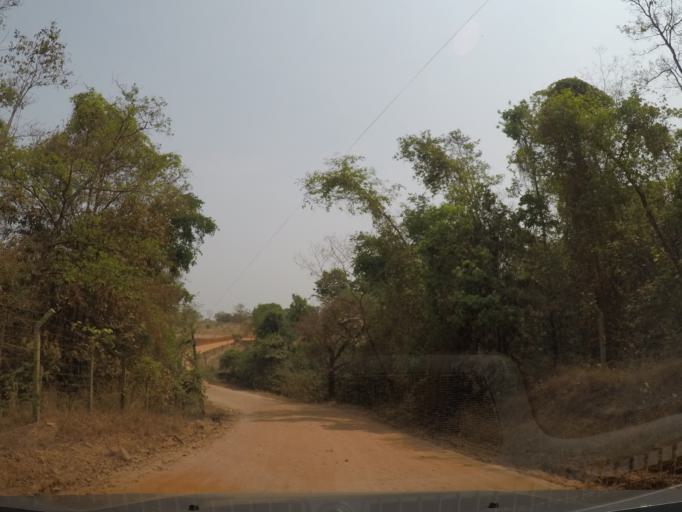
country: BR
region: Goias
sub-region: Pirenopolis
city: Pirenopolis
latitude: -15.8359
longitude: -48.9521
